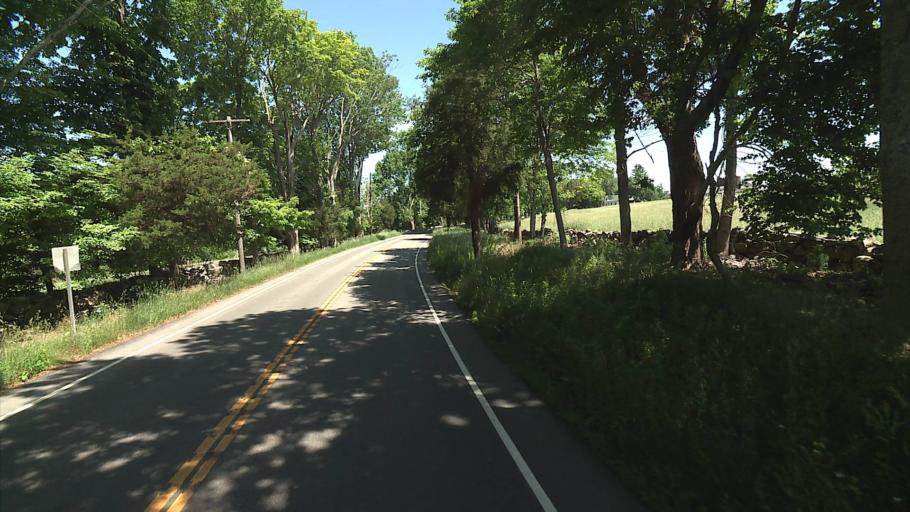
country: US
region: Rhode Island
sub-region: Washington County
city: Hopkinton
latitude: 41.5130
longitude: -71.8416
